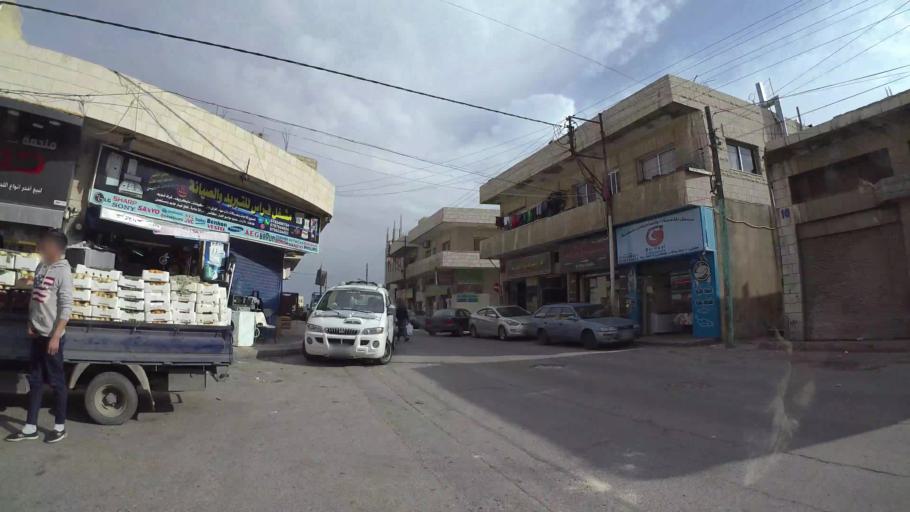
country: JO
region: Amman
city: Amman
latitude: 31.9991
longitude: 35.9456
